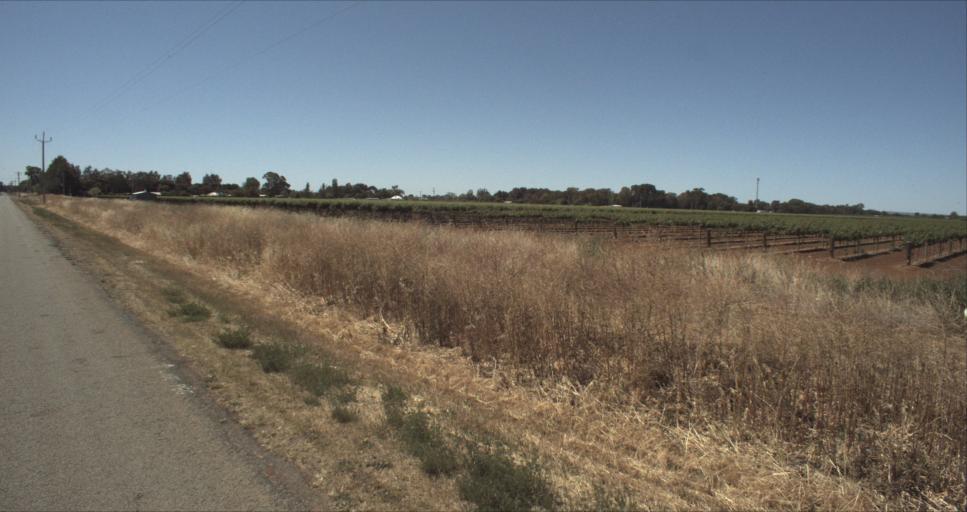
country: AU
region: New South Wales
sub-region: Leeton
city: Leeton
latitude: -34.5332
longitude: 146.3286
